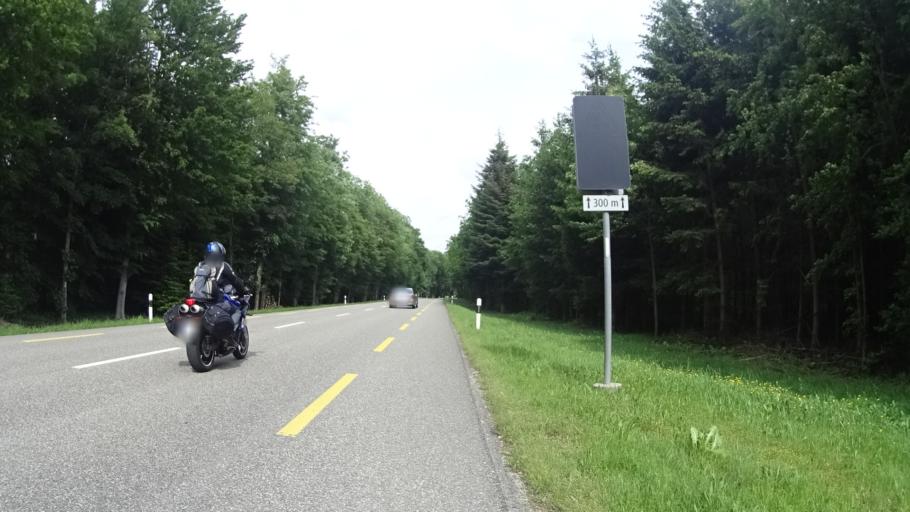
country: DE
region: Baden-Wuerttemberg
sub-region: Freiburg Region
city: Murg
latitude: 47.5532
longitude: 8.0027
